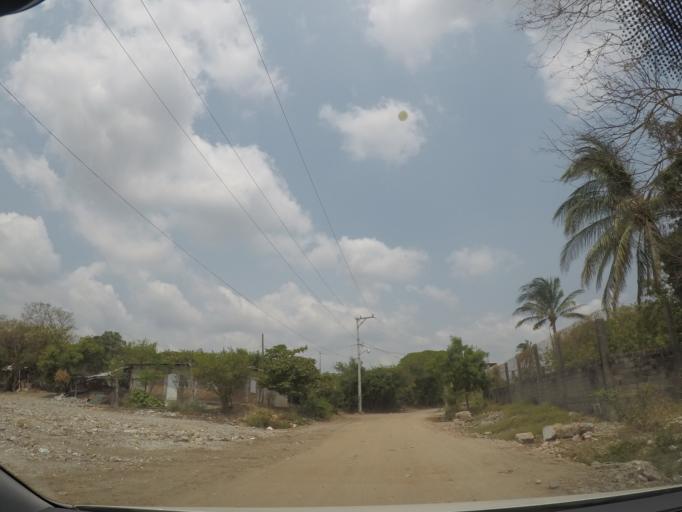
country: MX
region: Oaxaca
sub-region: El Espinal
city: El Espinal
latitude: 16.4763
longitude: -95.0437
